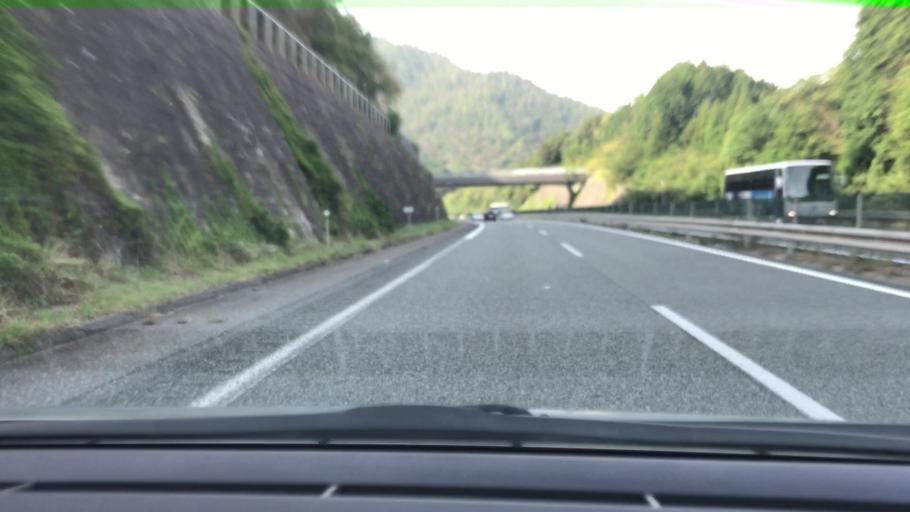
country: JP
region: Hyogo
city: Sasayama
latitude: 35.0187
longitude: 135.1748
